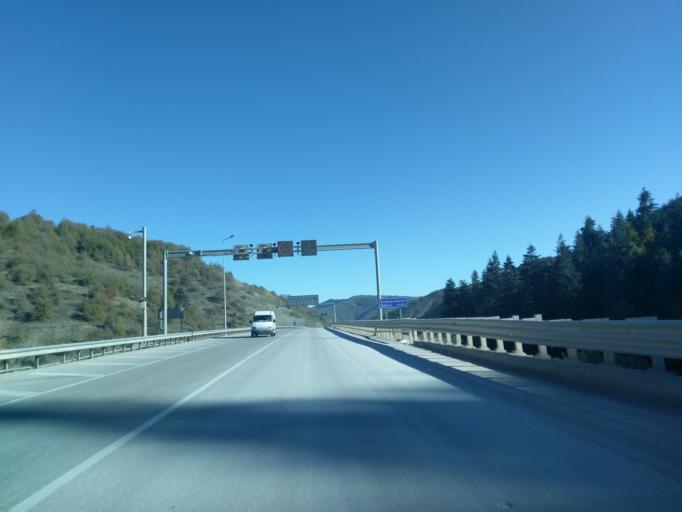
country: TR
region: Sinop
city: Boyabat
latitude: 41.6399
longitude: 34.8950
